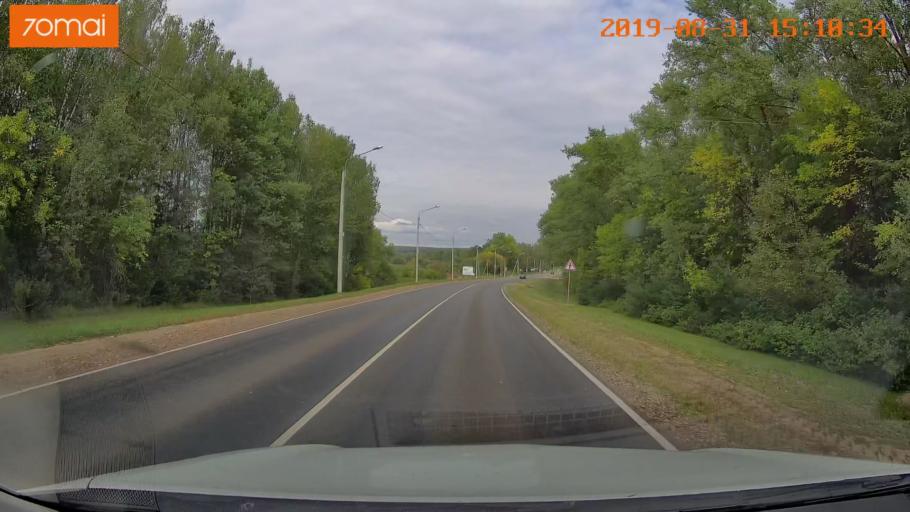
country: RU
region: Kaluga
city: Spas-Demensk
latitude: 54.4149
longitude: 34.2226
